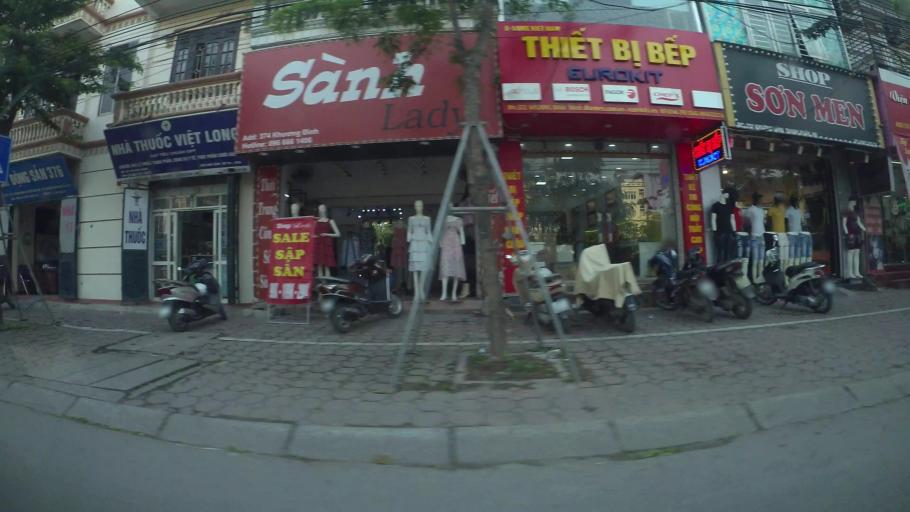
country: VN
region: Ha Noi
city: Thanh Xuan
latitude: 20.9886
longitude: 105.8129
